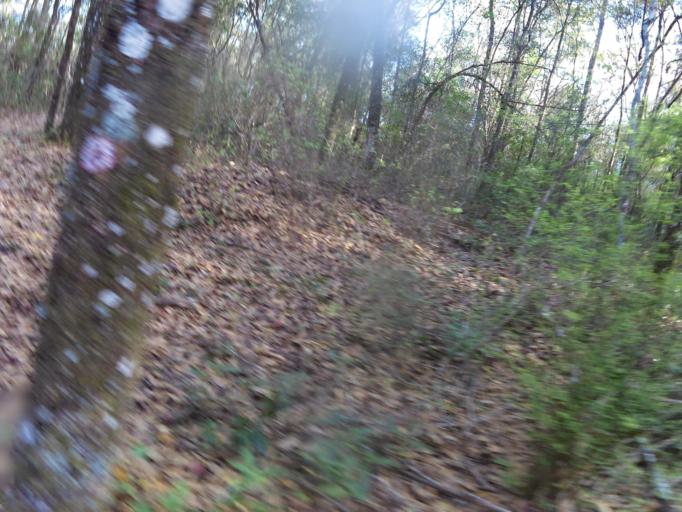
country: US
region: Florida
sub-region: Clay County
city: Middleburg
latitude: 30.1518
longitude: -81.9561
